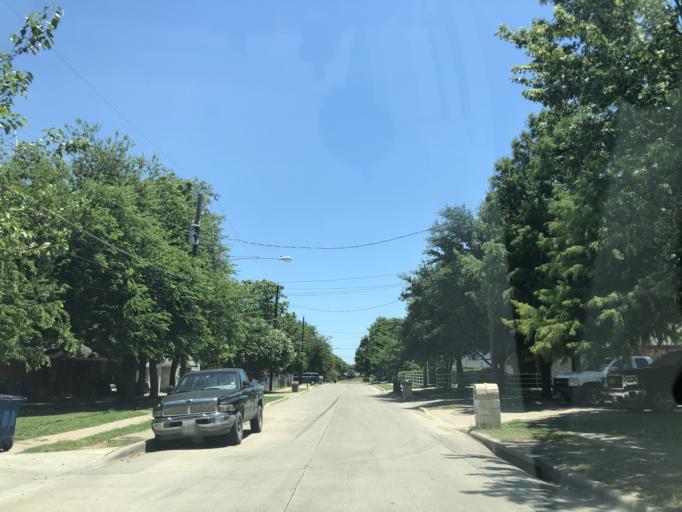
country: US
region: Texas
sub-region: Dallas County
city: Irving
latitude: 32.7944
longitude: -96.8948
